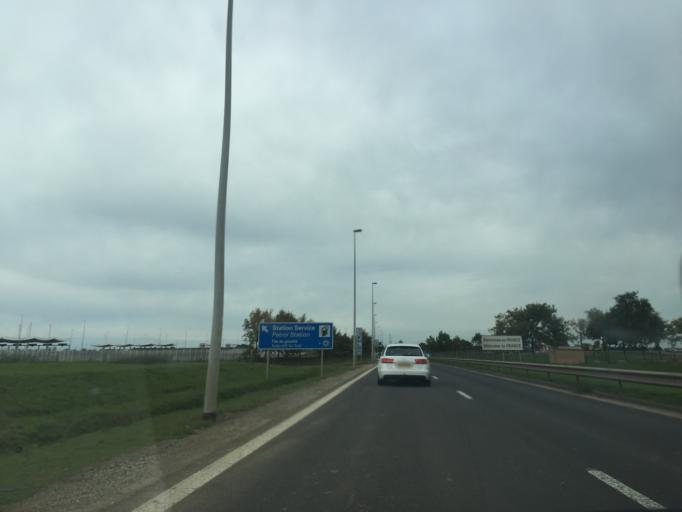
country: FR
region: Nord-Pas-de-Calais
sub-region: Departement du Pas-de-Calais
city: Frethun
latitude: 50.9310
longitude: 1.8174
